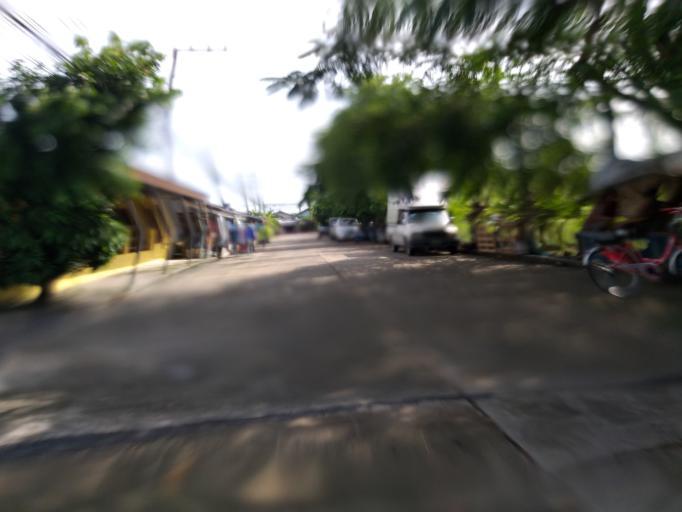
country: TH
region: Pathum Thani
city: Nong Suea
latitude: 14.0550
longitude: 100.8553
